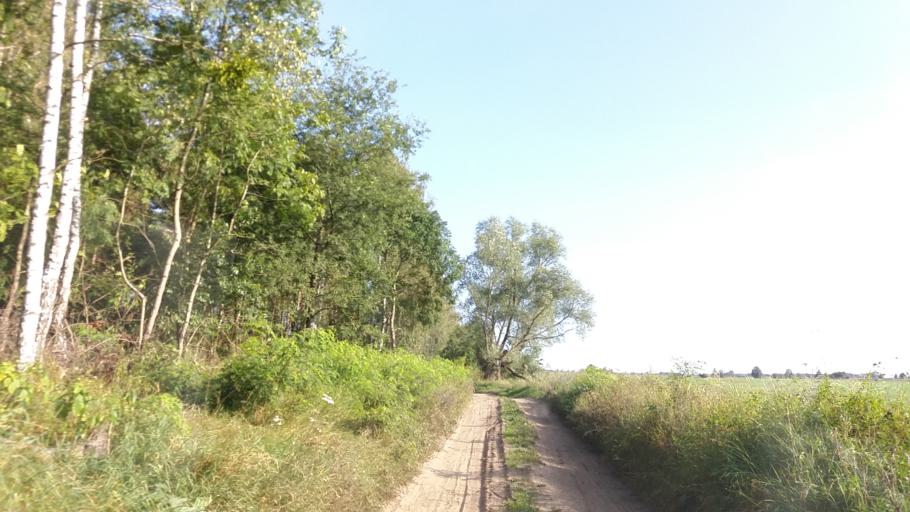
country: PL
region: West Pomeranian Voivodeship
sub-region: Powiat choszczenski
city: Recz
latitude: 53.2053
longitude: 15.5425
